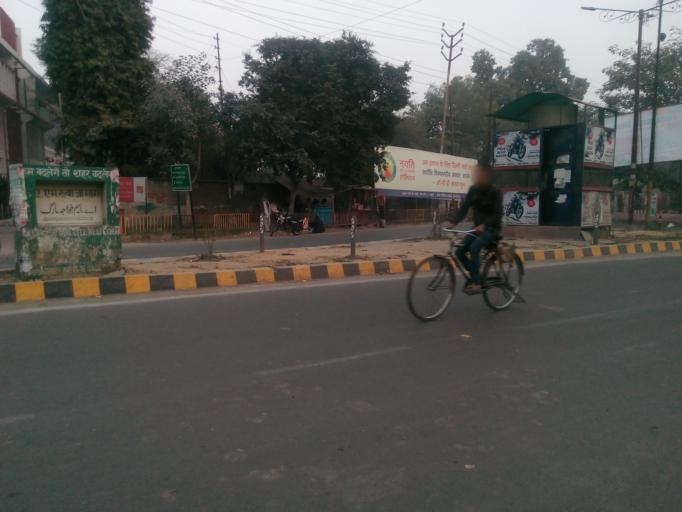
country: IN
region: Uttar Pradesh
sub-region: Aligarh
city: Aligarh
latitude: 27.9001
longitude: 78.0724
